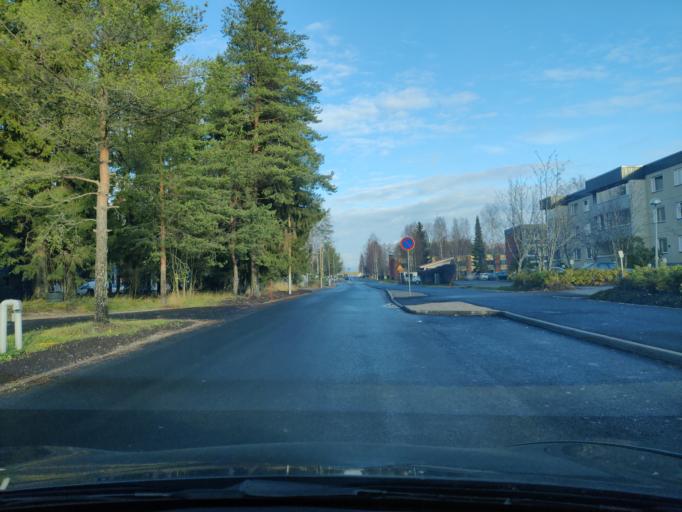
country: FI
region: Northern Savo
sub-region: Ylae-Savo
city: Kiuruvesi
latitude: 63.6451
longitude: 26.6307
